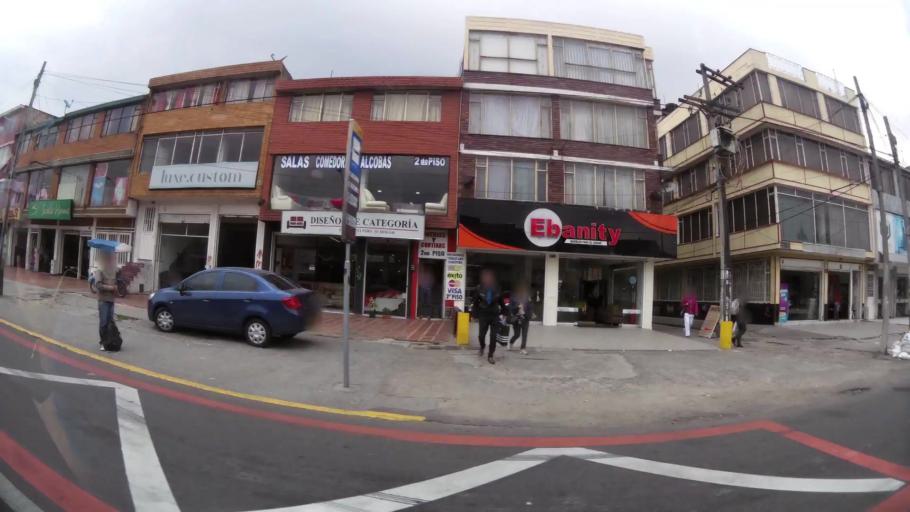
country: CO
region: Bogota D.C.
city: Bogota
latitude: 4.6018
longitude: -74.1198
